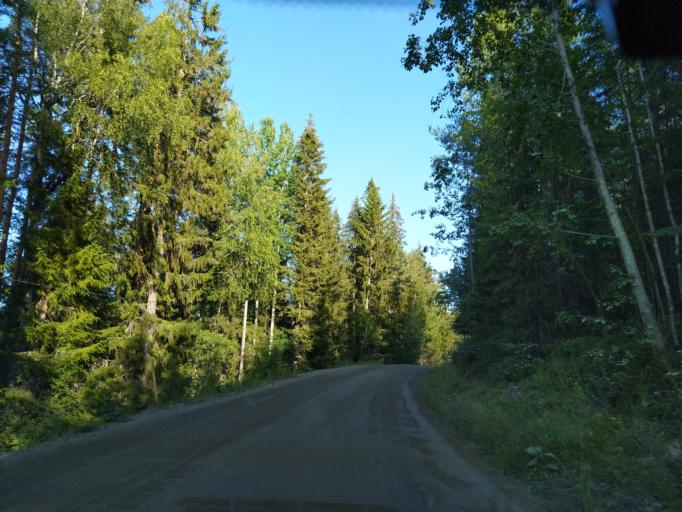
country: FI
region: Central Finland
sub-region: Jaemsae
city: Kuhmoinen
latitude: 61.6106
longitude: 25.1226
